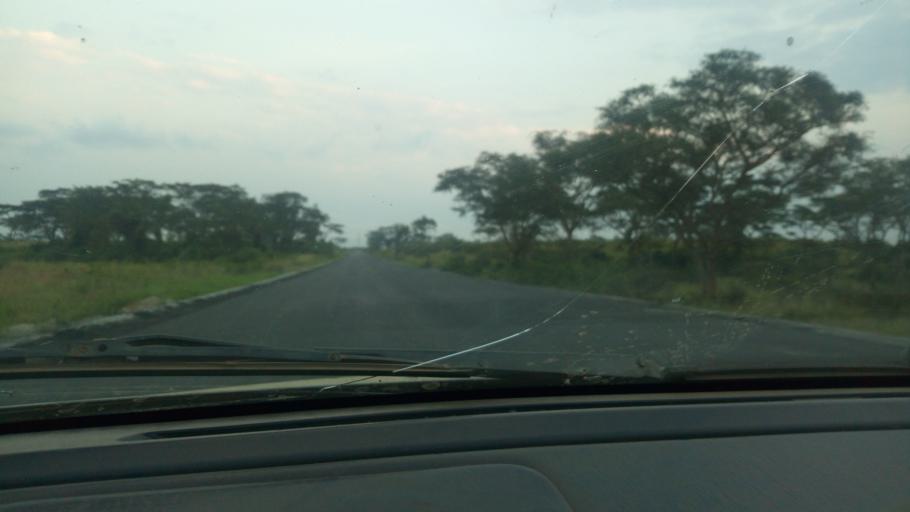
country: UG
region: Western Region
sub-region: Rubirizi District
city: Rubirizi
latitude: -0.1602
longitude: 30.0743
